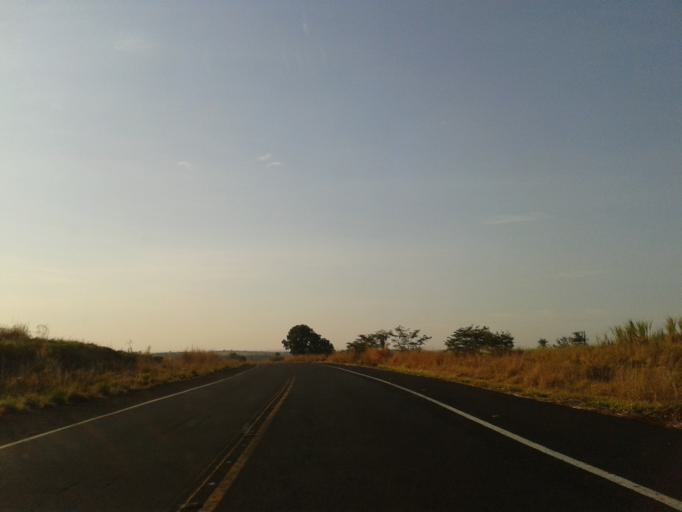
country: BR
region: Minas Gerais
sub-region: Santa Vitoria
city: Santa Vitoria
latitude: -19.1185
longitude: -50.3070
